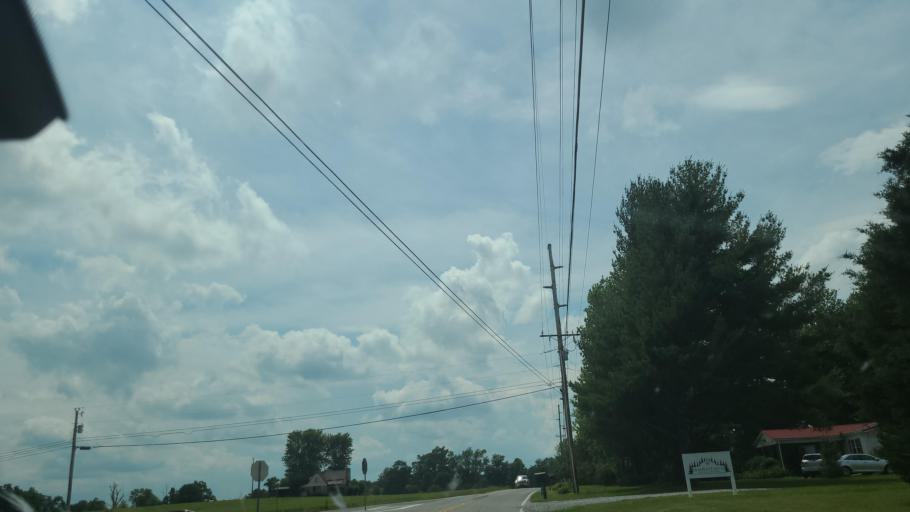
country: US
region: Tennessee
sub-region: Cumberland County
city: Crossville
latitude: 35.9071
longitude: -85.0278
